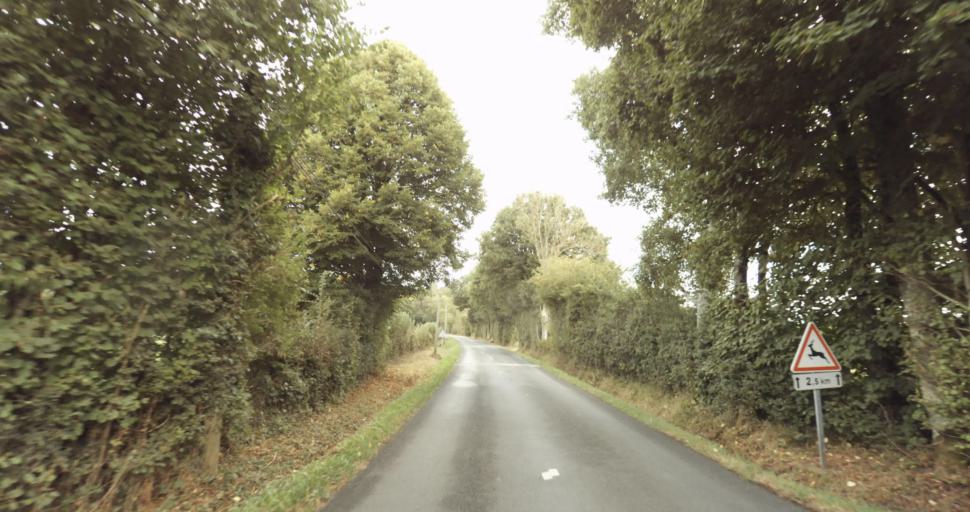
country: FR
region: Lower Normandy
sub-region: Departement de l'Orne
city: Gace
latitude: 48.7965
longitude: 0.2596
